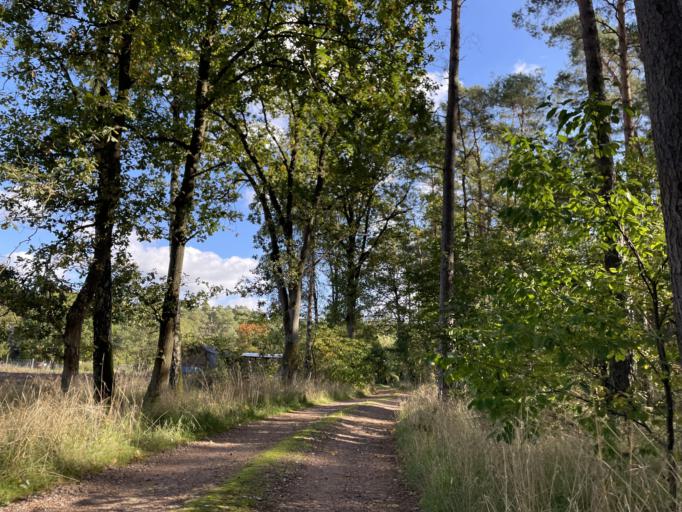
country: DE
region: Lower Saxony
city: Barendorf
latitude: 53.2171
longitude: 10.5001
